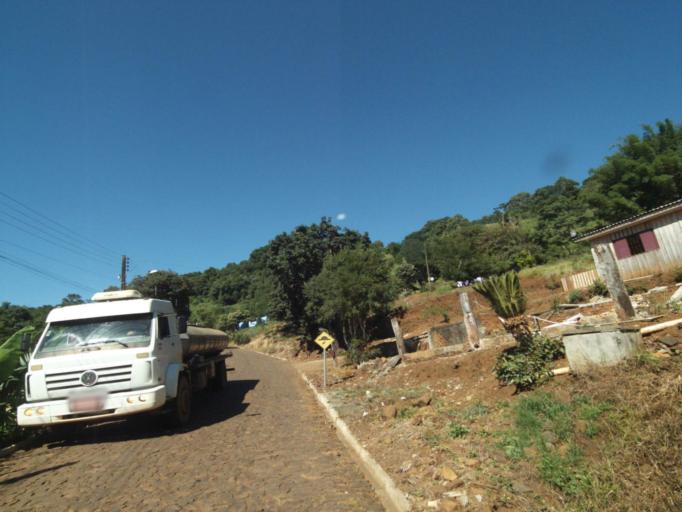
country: BR
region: Parana
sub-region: Ampere
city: Ampere
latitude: -26.1696
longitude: -53.3606
